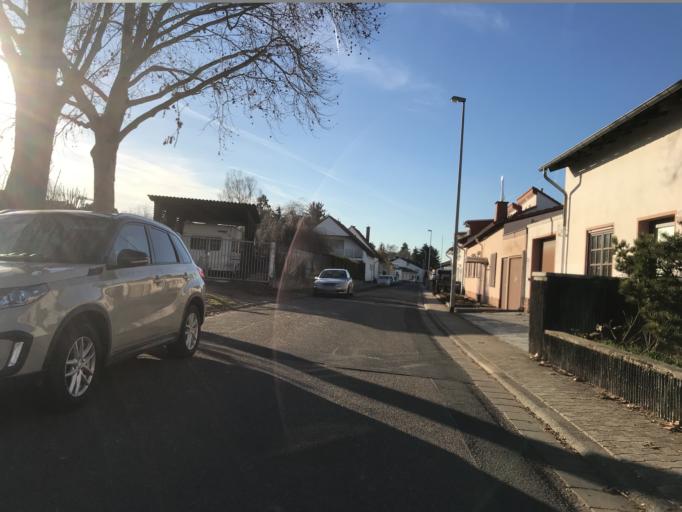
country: DE
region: Rheinland-Pfalz
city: Mainz
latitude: 49.9689
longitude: 8.2921
